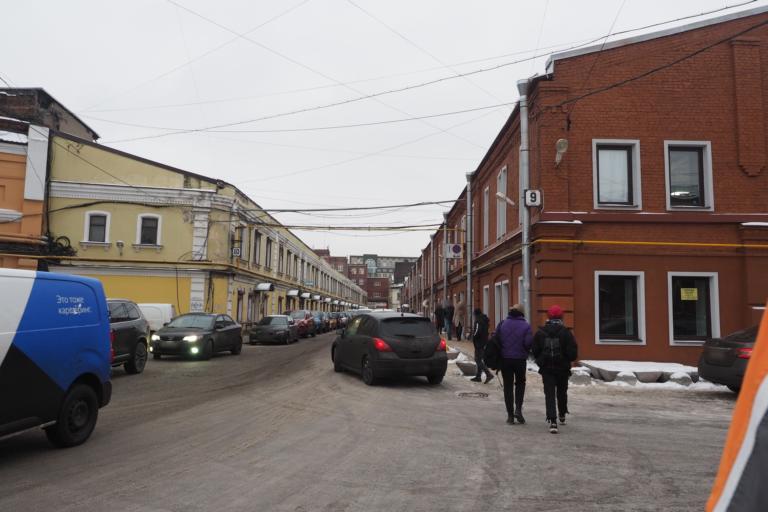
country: RU
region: St.-Petersburg
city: Centralniy
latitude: 59.9244
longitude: 30.3622
